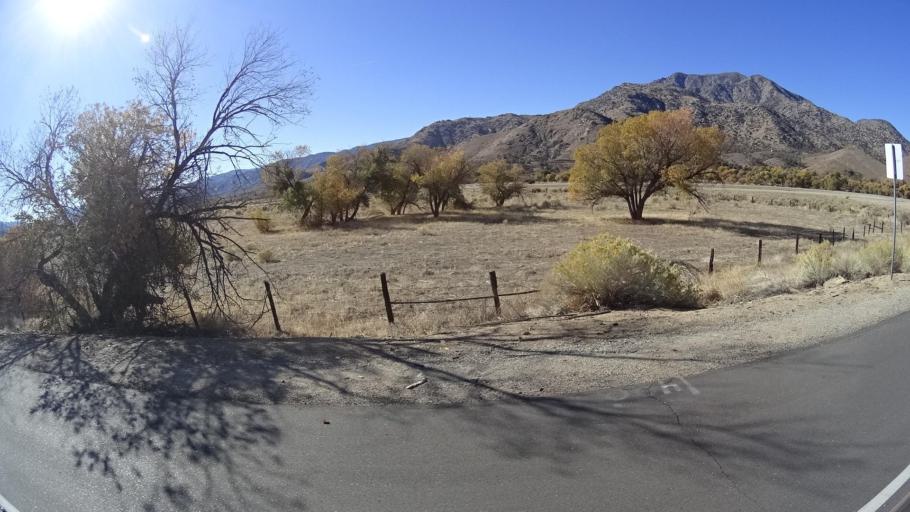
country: US
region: California
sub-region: Kern County
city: Kernville
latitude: 35.7312
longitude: -118.4165
